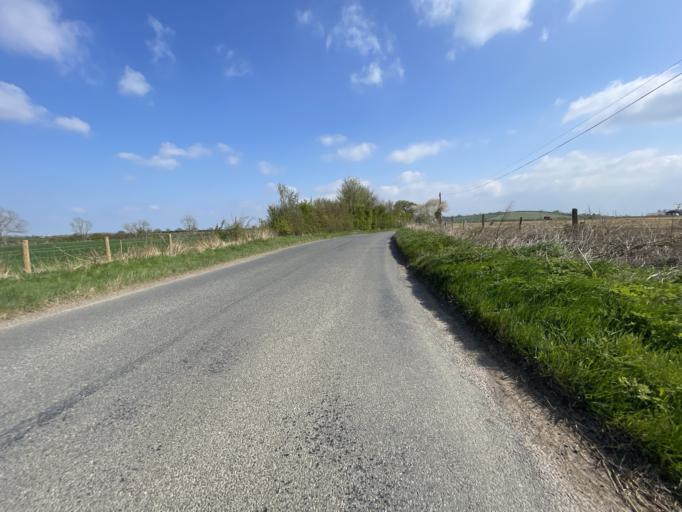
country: GB
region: England
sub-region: Warwickshire
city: Rugby
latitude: 52.3434
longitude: -1.2371
